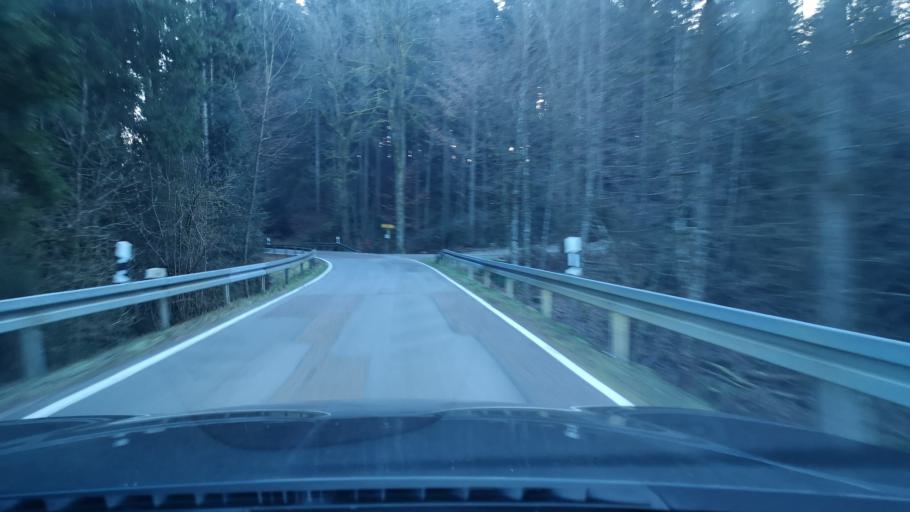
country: DE
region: Baden-Wuerttemberg
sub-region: Regierungsbezirk Stuttgart
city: Gschwend
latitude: 48.9353
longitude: 9.7018
